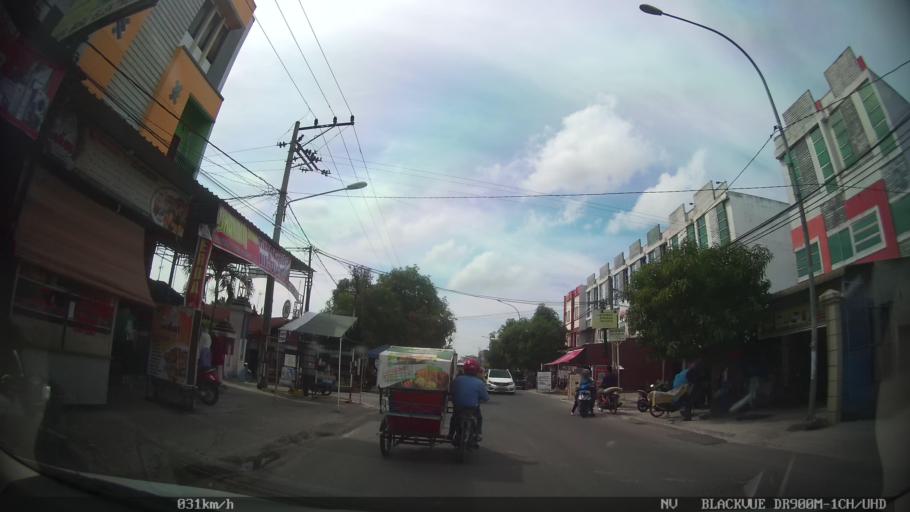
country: ID
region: North Sumatra
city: Percut
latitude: 3.5726
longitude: 98.8690
